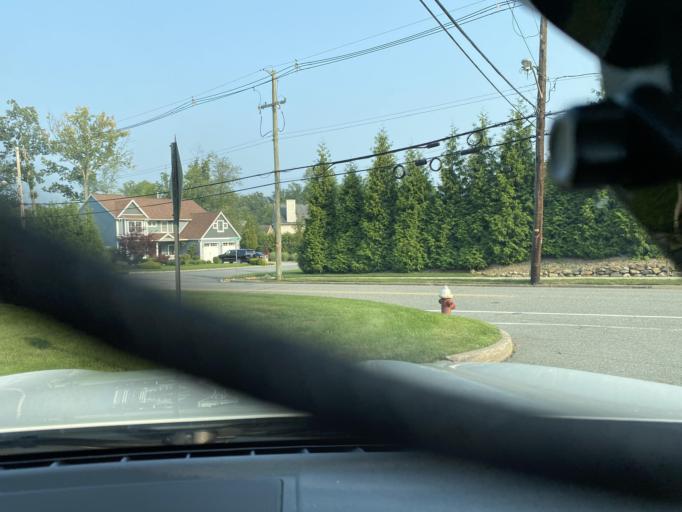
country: US
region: New Jersey
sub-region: Bergen County
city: Mahwah
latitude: 41.0895
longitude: -74.1308
